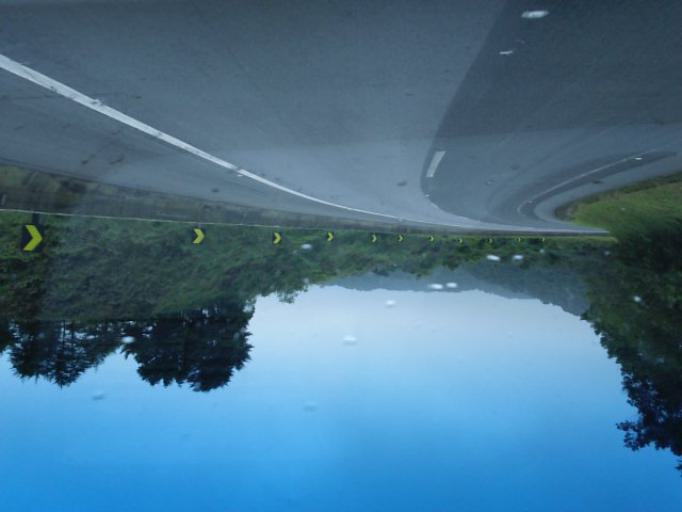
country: BR
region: Sao Paulo
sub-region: Cajati
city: Cajati
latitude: -24.9644
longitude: -48.4253
